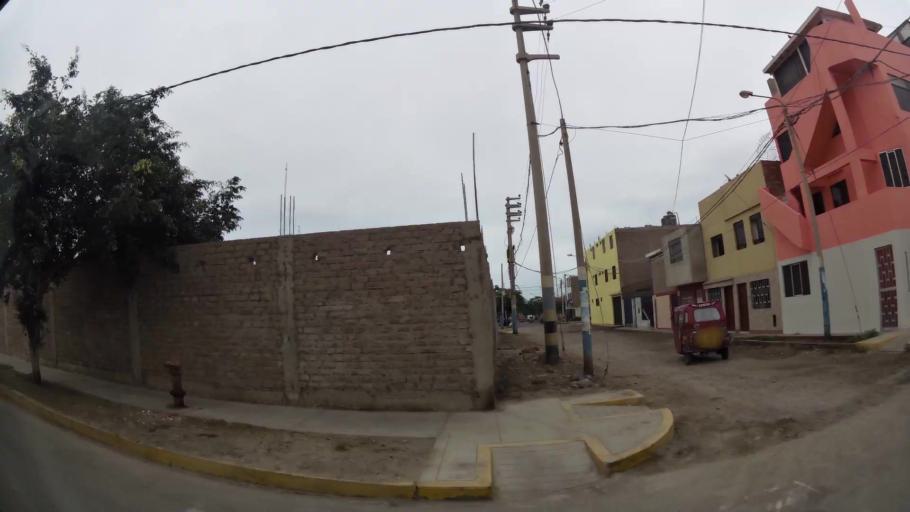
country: PE
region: Ica
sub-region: Provincia de Pisco
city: Pisco
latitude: -13.7064
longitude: -76.2046
